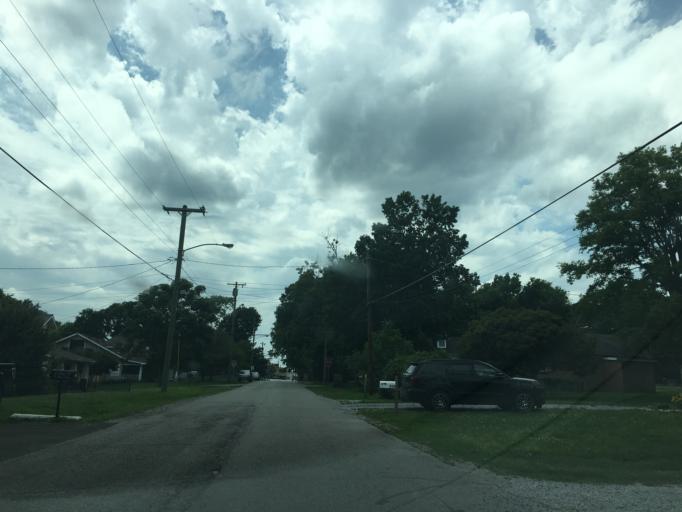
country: US
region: Tennessee
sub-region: Davidson County
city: Oak Hill
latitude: 36.1176
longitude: -86.7449
